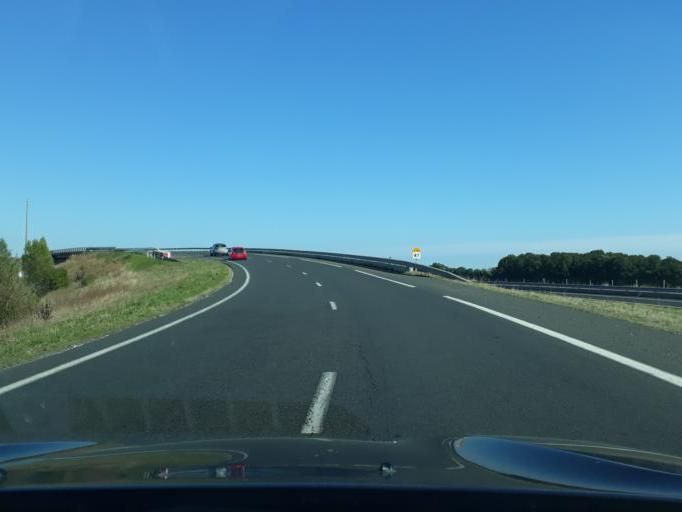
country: FR
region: Centre
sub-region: Departement d'Indre-et-Loire
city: Artannes-sur-Indre
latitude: 47.3038
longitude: 0.5646
